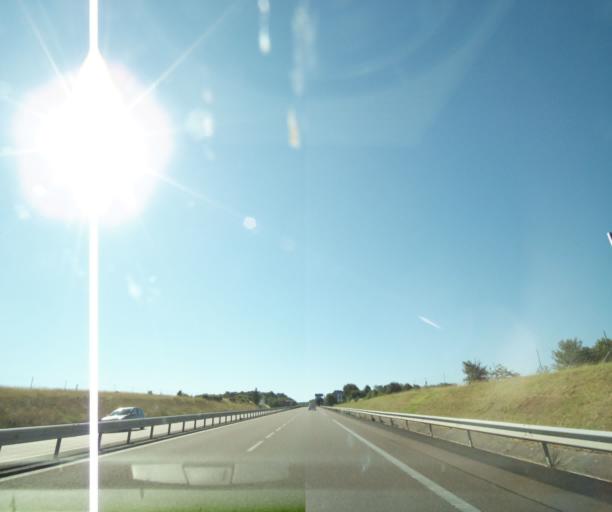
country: FR
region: Champagne-Ardenne
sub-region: Departement de la Haute-Marne
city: Chateauvillain
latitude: 48.0598
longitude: 4.9518
